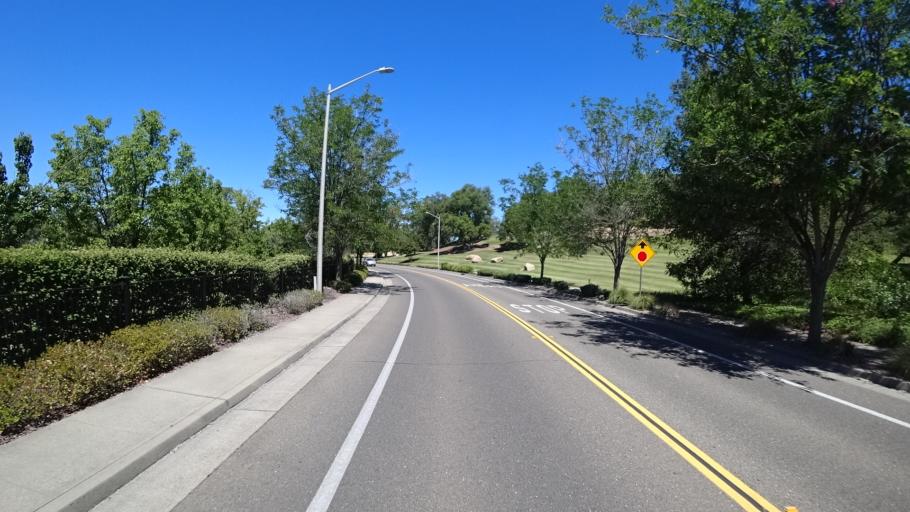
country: US
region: California
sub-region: Placer County
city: Rocklin
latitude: 38.8223
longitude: -121.2425
